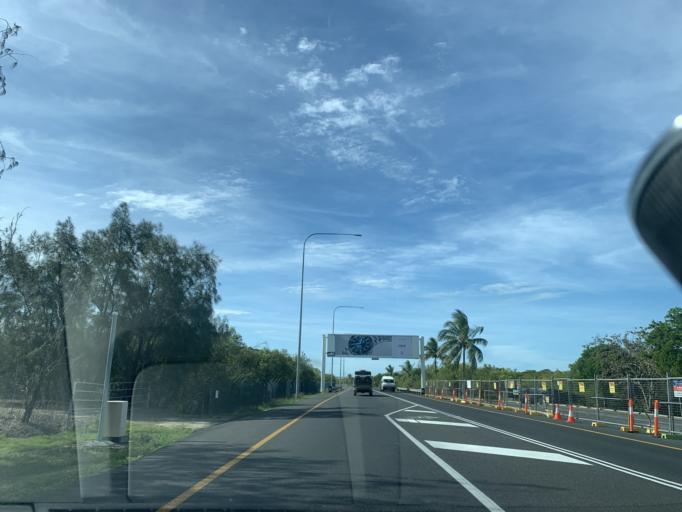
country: AU
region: Queensland
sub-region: Cairns
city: Cairns
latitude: -16.8840
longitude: 145.7611
